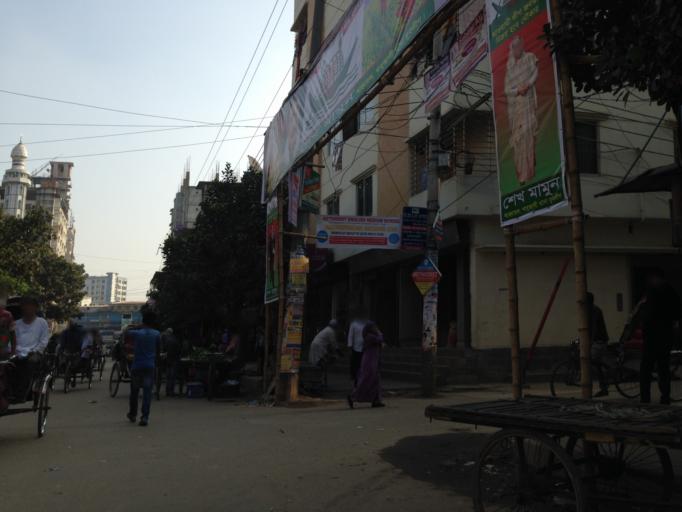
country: BD
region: Dhaka
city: Azimpur
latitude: 23.7998
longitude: 90.3509
